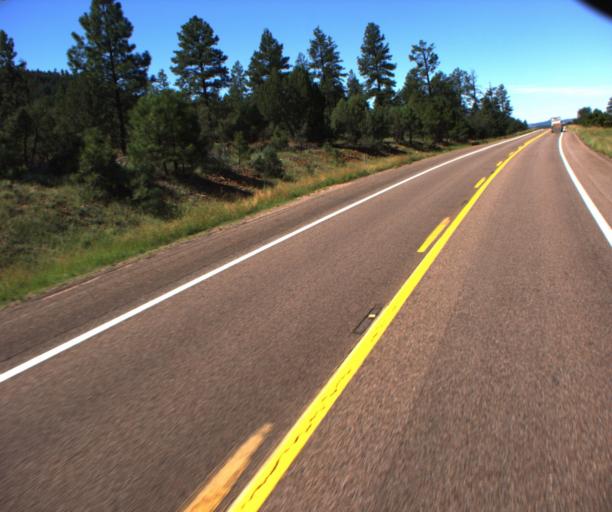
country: US
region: Arizona
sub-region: Navajo County
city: Linden
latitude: 34.0569
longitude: -110.2124
